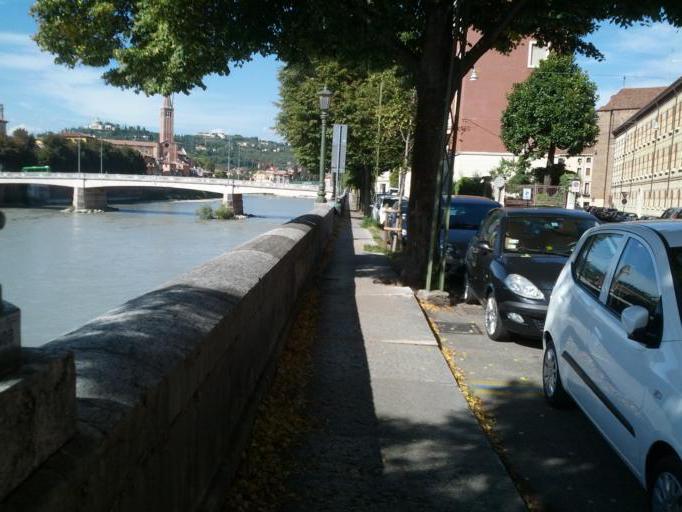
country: IT
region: Veneto
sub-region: Provincia di Verona
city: Verona
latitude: 45.4411
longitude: 11.0022
